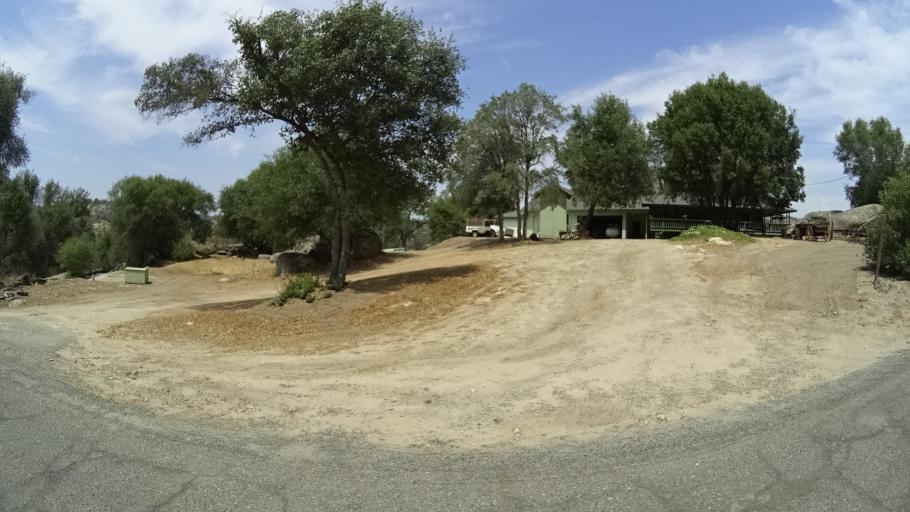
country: US
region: California
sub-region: Madera County
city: Ahwahnee
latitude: 37.3966
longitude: -119.8318
